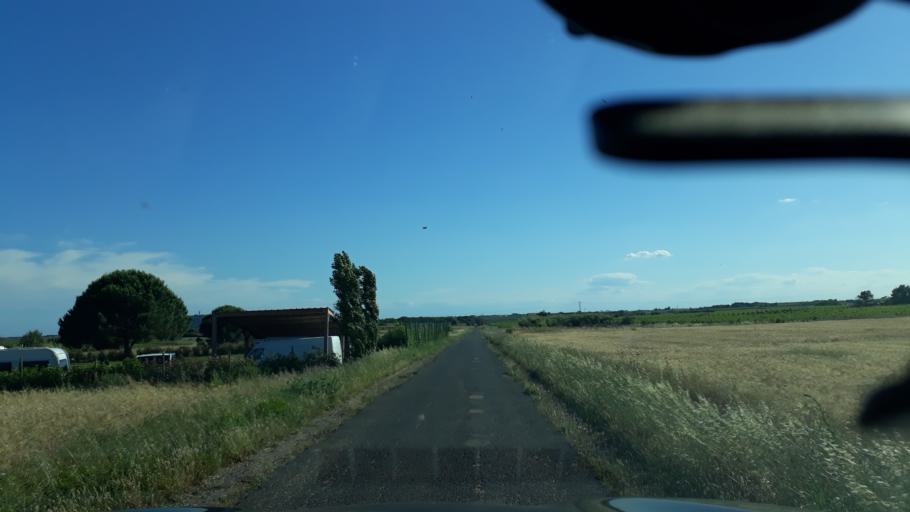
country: FR
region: Languedoc-Roussillon
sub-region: Departement de l'Herault
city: Marseillan
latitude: 43.3450
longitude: 3.5129
